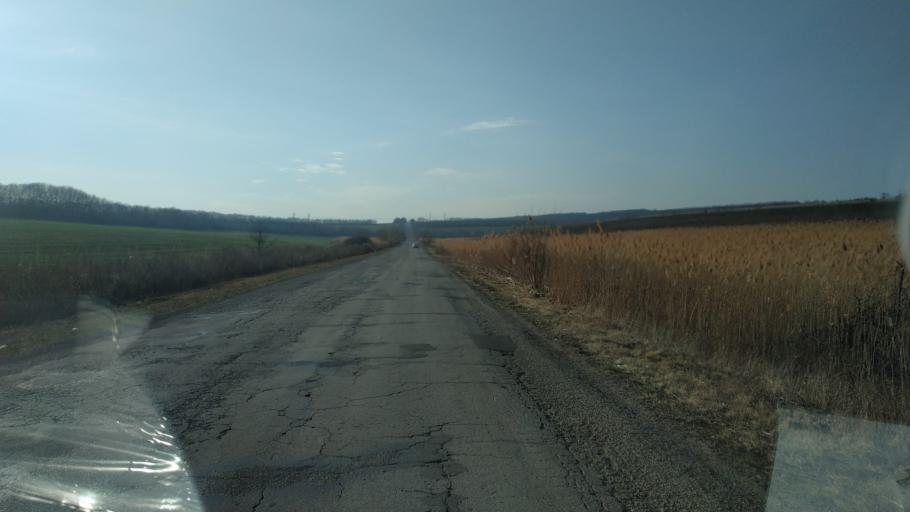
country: MD
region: Chisinau
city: Singera
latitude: 46.8853
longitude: 29.0394
